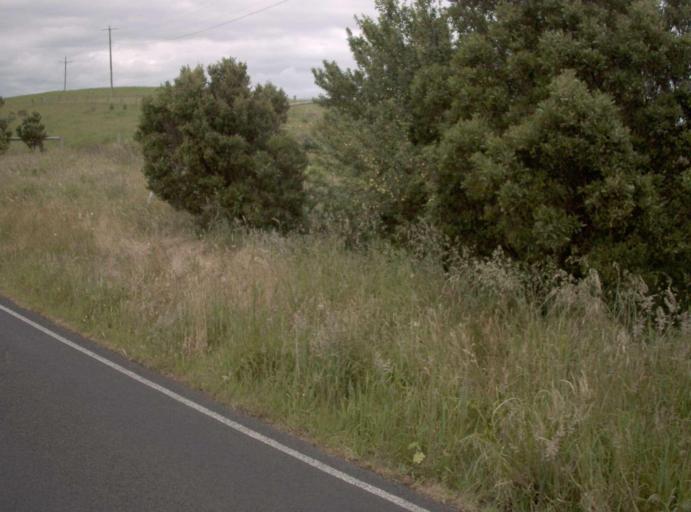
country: AU
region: Victoria
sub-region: Bass Coast
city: North Wonthaggi
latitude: -38.5020
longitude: 145.7260
